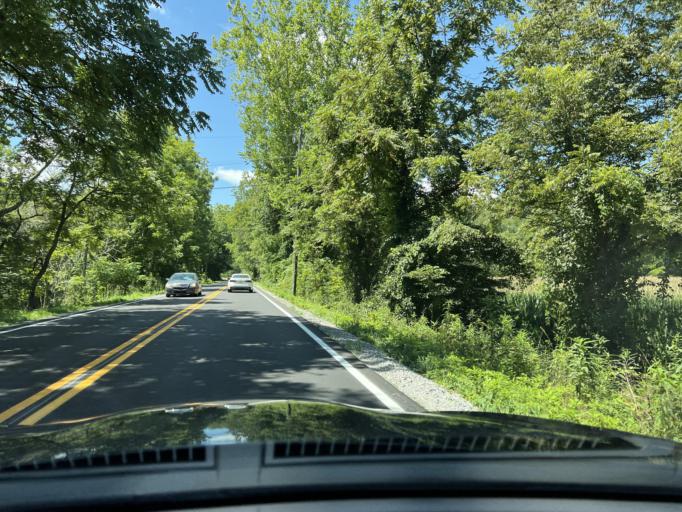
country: US
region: North Carolina
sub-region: Buncombe County
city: Fairview
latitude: 35.4946
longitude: -82.4285
